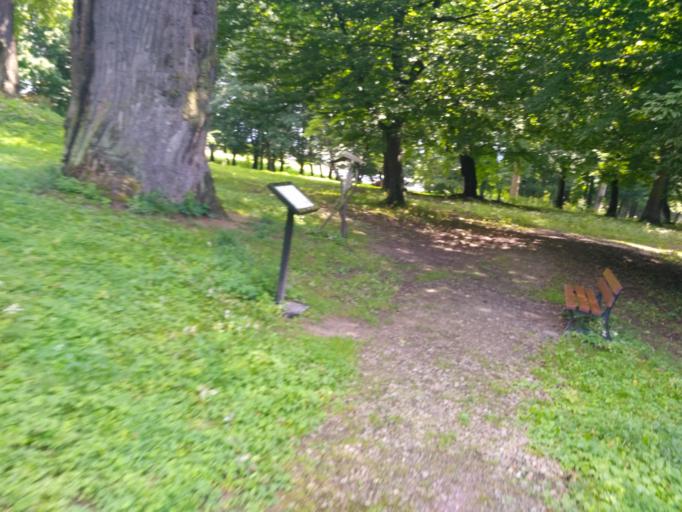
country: PL
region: Subcarpathian Voivodeship
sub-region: Powiat strzyzowski
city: Wisniowa
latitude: 49.8687
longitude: 21.6440
